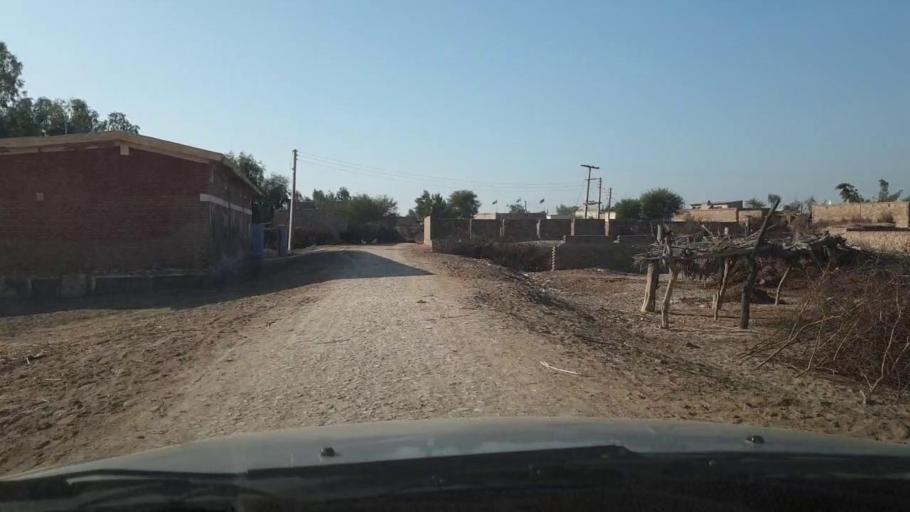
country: PK
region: Sindh
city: Mirpur Mathelo
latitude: 27.9828
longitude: 69.5307
